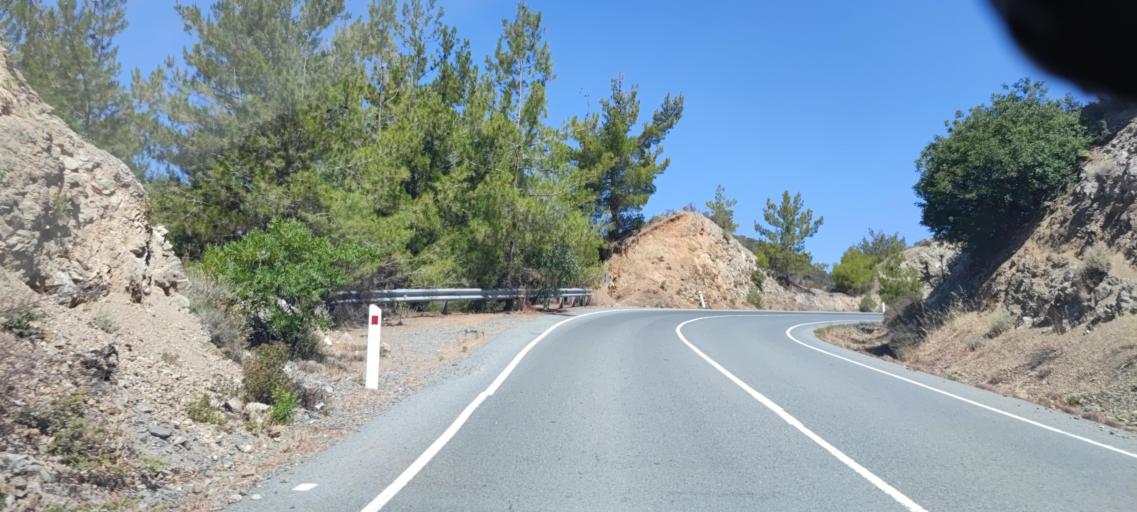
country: CY
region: Limassol
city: Pachna
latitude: 34.9006
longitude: 32.8152
